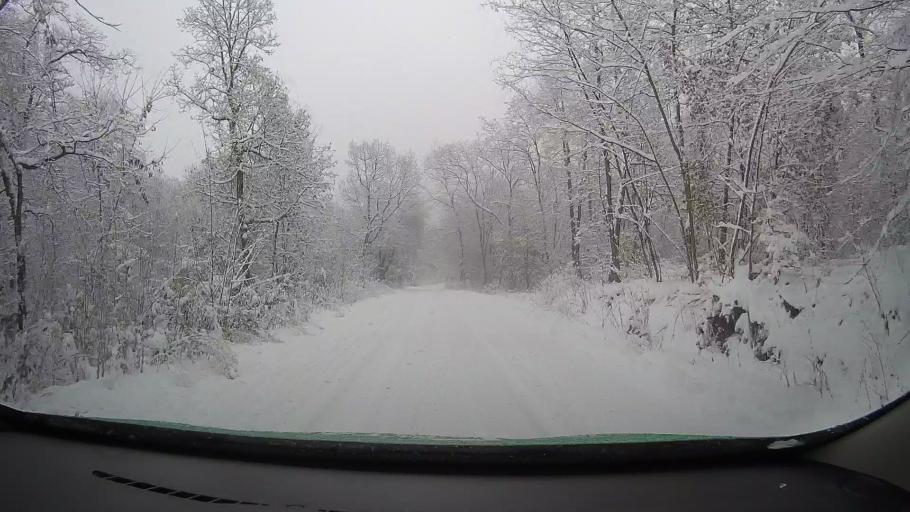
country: RO
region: Hunedoara
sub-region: Comuna Teliucu Inferior
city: Teliucu Inferior
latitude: 45.6892
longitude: 22.8972
